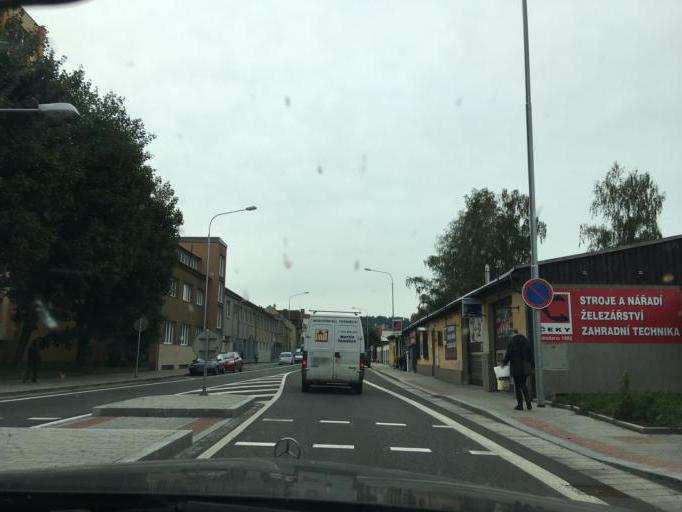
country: CZ
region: Kralovehradecky
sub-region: Okres Nachod
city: Nachod
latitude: 50.4170
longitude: 16.1741
